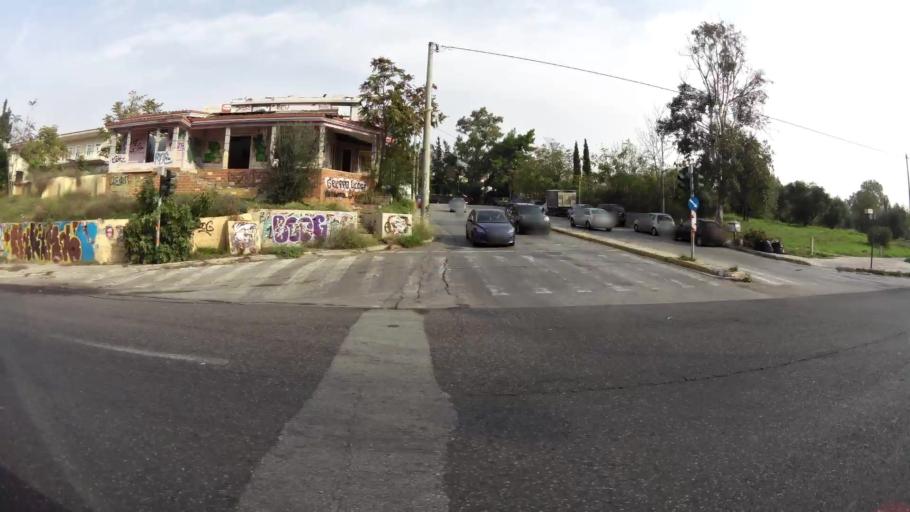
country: GR
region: Attica
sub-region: Nomarchia Athinas
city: Chaidari
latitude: 38.0129
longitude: 23.6387
